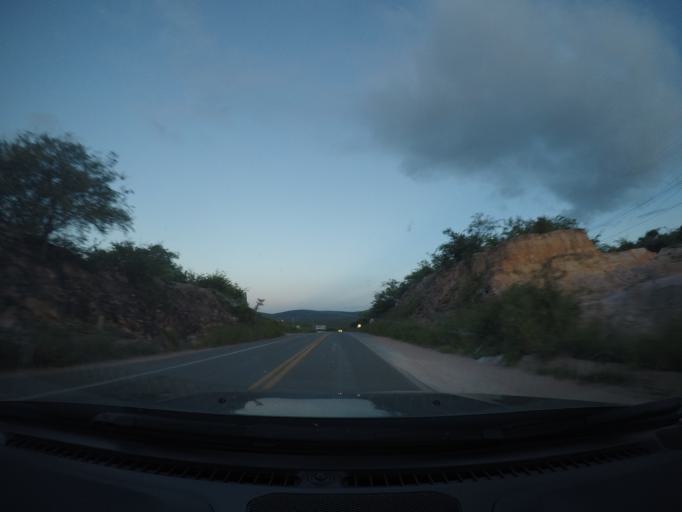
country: BR
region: Bahia
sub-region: Seabra
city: Seabra
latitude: -12.4268
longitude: -41.7663
